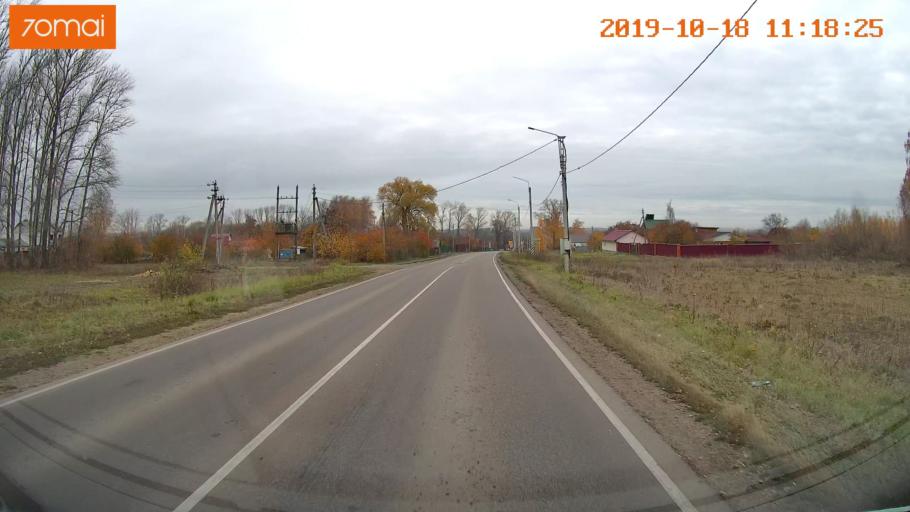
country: RU
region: Tula
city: Kimovsk
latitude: 54.0388
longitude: 38.5503
